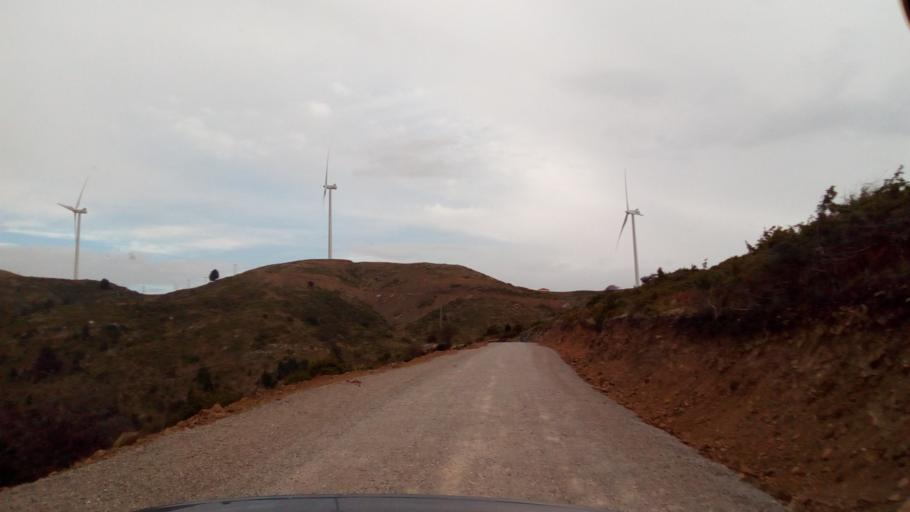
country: GR
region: Central Greece
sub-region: Nomos Fokidos
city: Lidoriki
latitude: 38.4508
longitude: 22.0754
